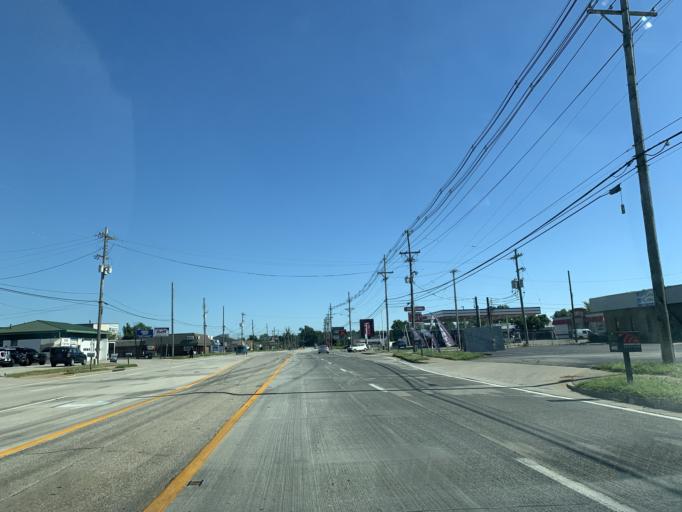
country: US
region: Kentucky
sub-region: Jefferson County
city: Audubon Park
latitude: 38.1882
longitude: -85.7025
